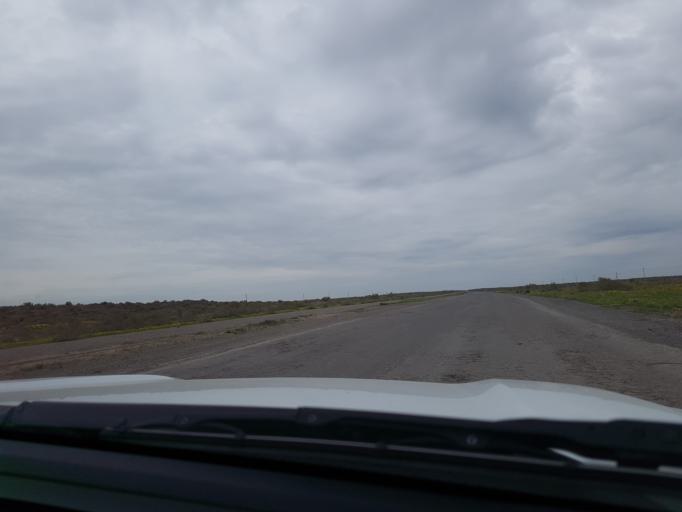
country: TM
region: Mary
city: Bayramaly
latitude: 37.9322
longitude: 62.6270
